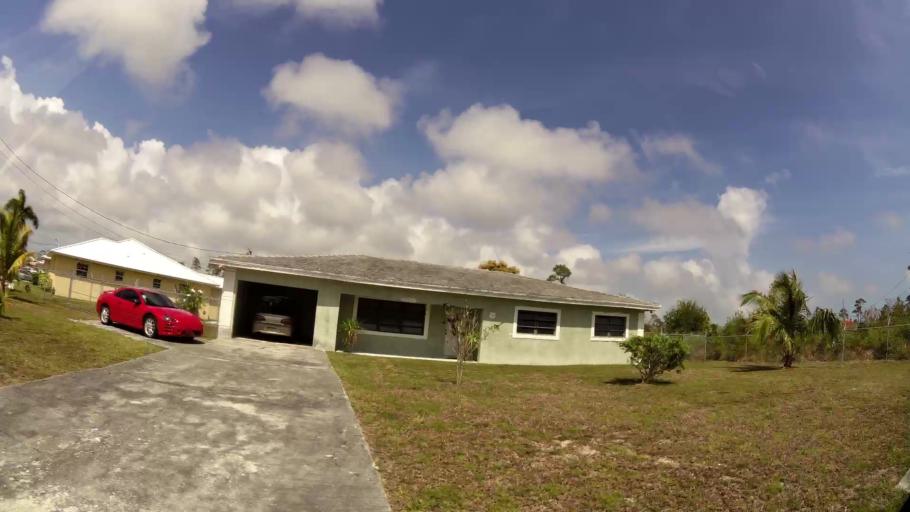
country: BS
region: Freeport
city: Freeport
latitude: 26.5032
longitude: -78.7267
